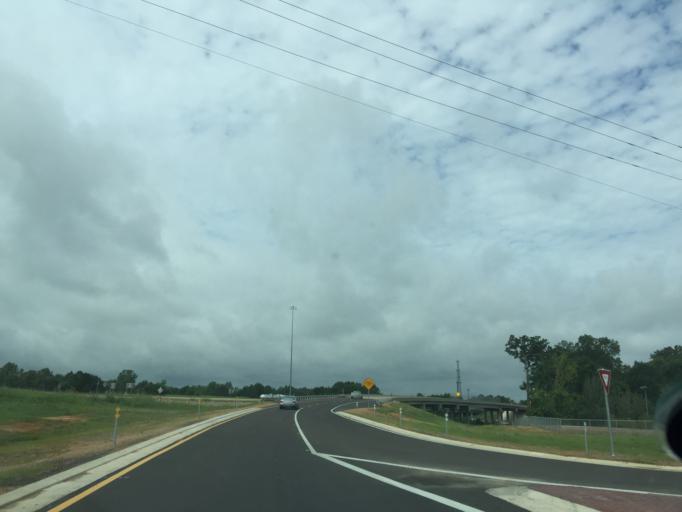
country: US
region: Mississippi
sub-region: Rankin County
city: Brandon
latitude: 32.2792
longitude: -90.0021
